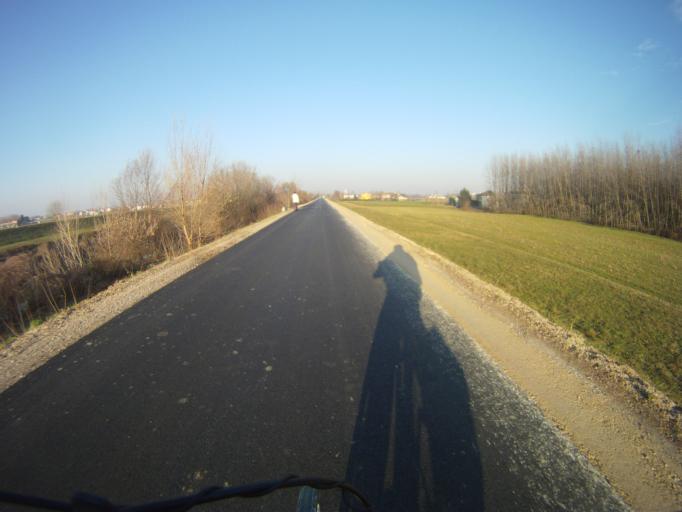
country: IT
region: Veneto
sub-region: Provincia di Padova
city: Legnaro
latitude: 45.3367
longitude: 11.9370
